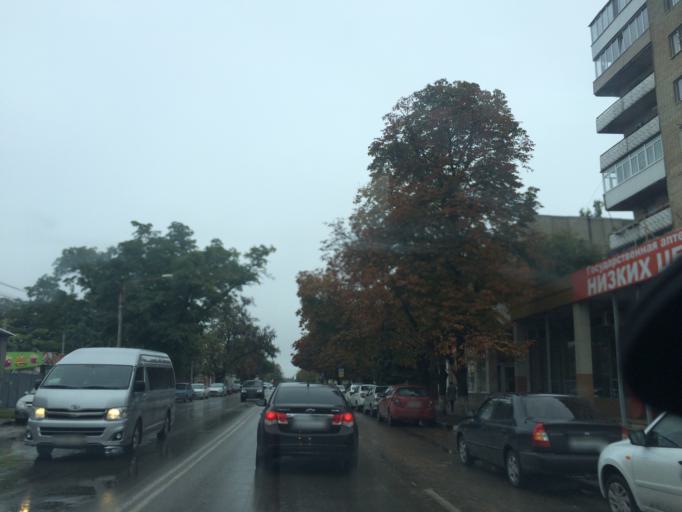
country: RU
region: Rostov
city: Azov
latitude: 47.1106
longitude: 39.4255
